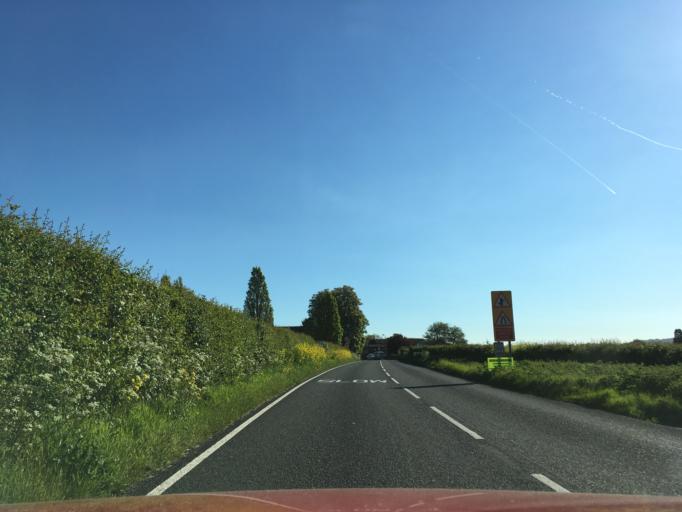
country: GB
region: England
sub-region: North Somerset
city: Clevedon
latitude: 51.4528
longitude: -2.8293
